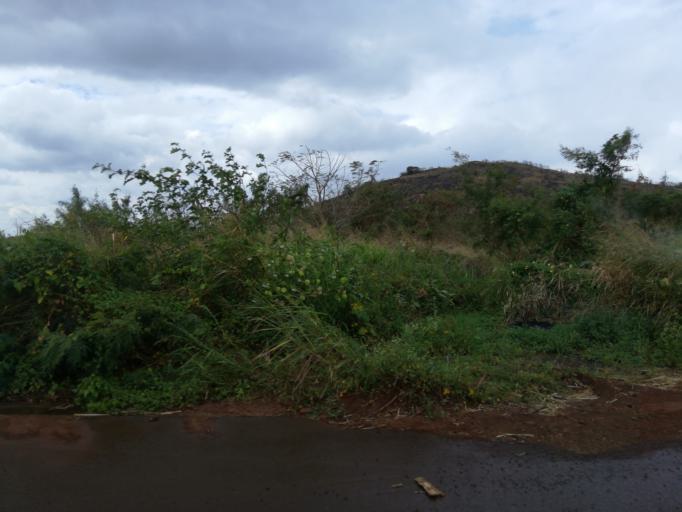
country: MU
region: Black River
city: Petite Riviere
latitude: -20.2086
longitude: 57.4584
